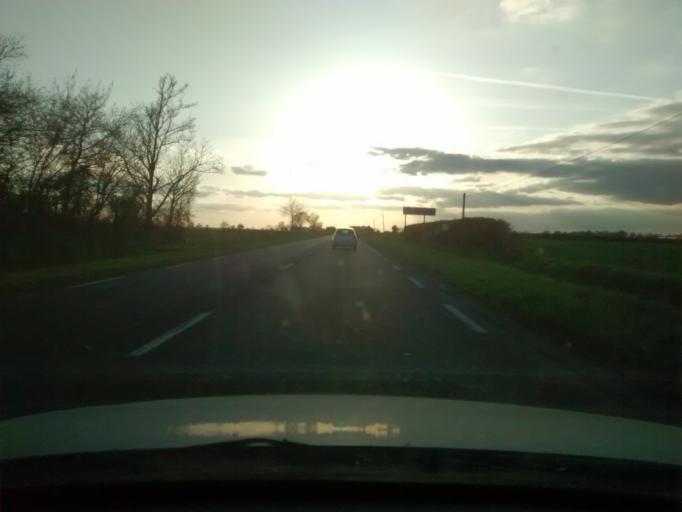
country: FR
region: Pays de la Loire
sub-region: Departement de la Mayenne
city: Sainte-Suzanne
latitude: 48.0326
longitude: -0.3393
